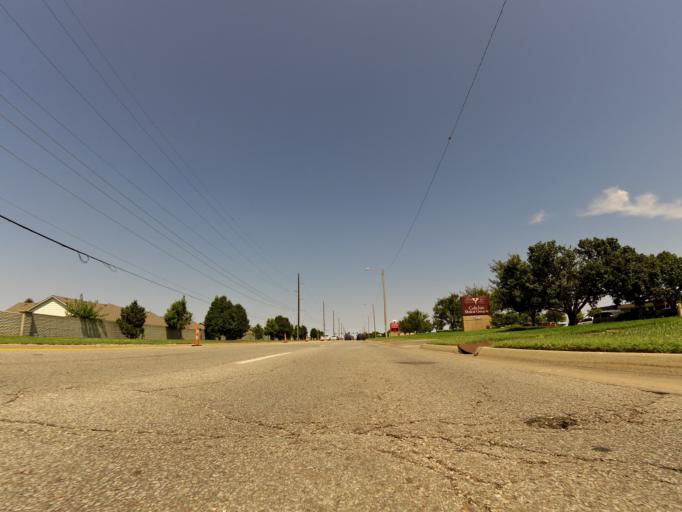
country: US
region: Kansas
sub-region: Sedgwick County
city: Bellaire
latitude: 37.7304
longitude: -97.2623
